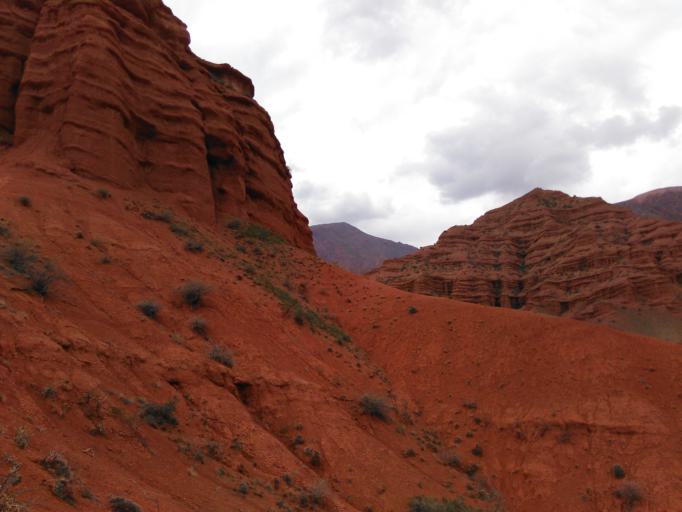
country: KG
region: Chuy
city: Bystrovka
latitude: 42.5925
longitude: 75.7795
